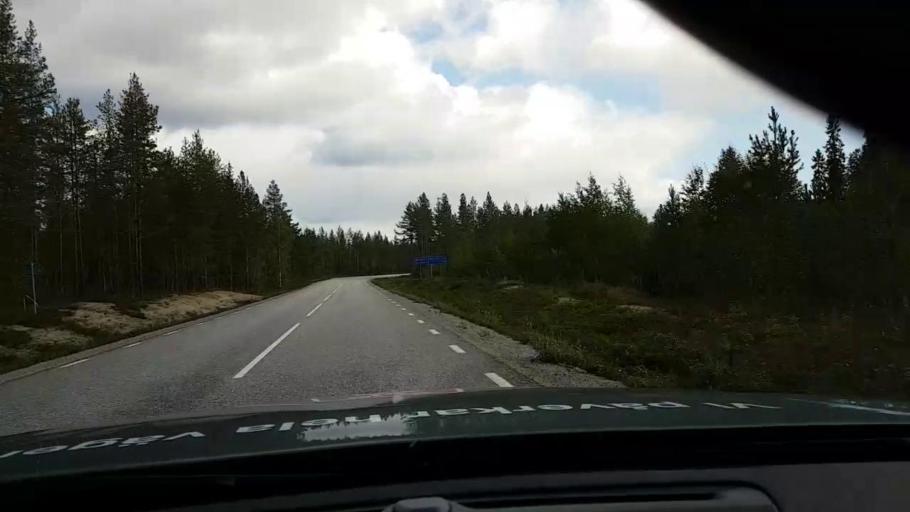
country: SE
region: Vaesternorrland
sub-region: OErnskoeldsviks Kommun
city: Bredbyn
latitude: 63.6855
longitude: 17.7737
